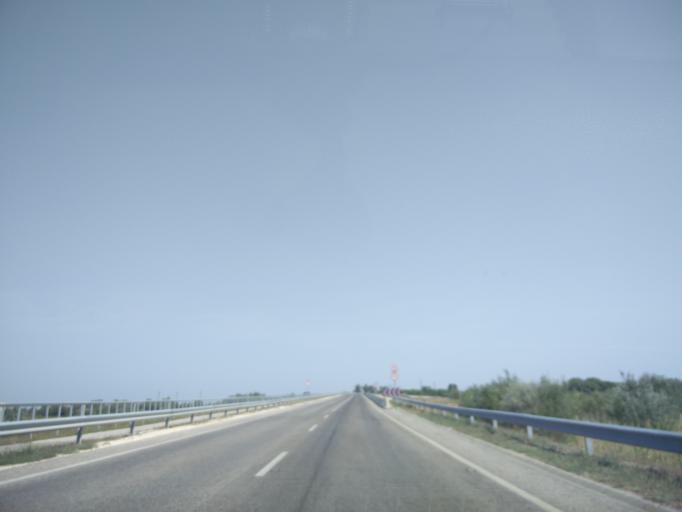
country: HU
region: Csongrad
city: Szeged
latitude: 46.2764
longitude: 20.0812
